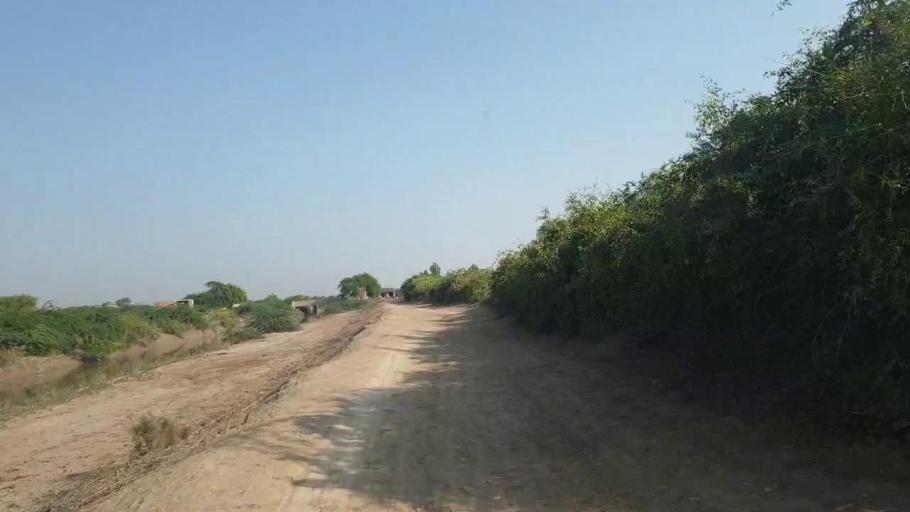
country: PK
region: Sindh
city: Badin
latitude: 24.4669
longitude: 68.7393
